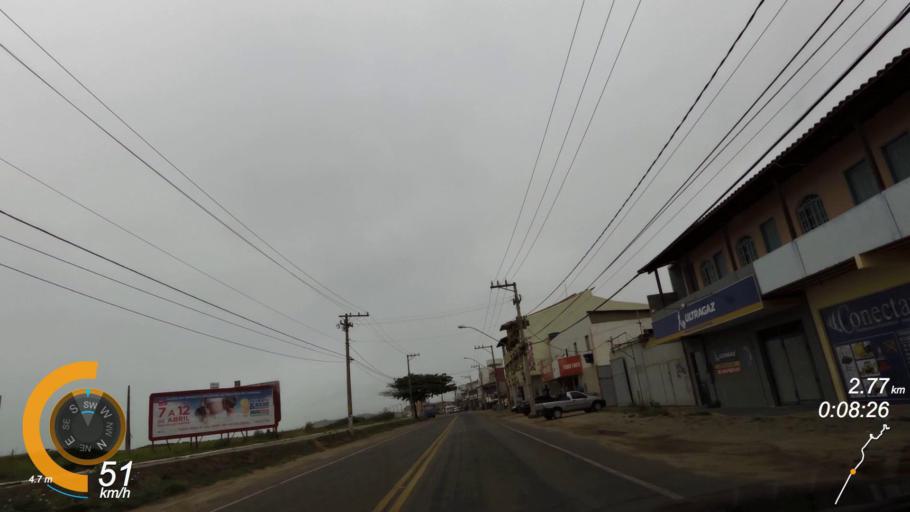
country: BR
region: Espirito Santo
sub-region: Guarapari
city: Guarapari
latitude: -20.6838
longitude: -40.5071
